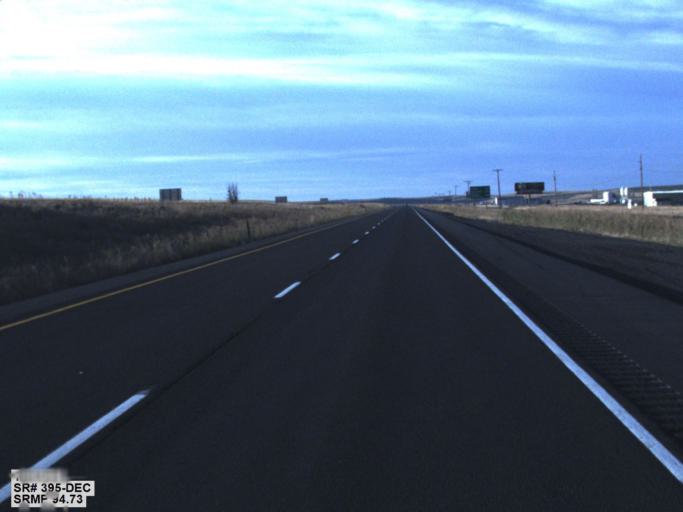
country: US
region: Washington
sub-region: Adams County
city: Ritzville
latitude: 47.0990
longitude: -118.4088
